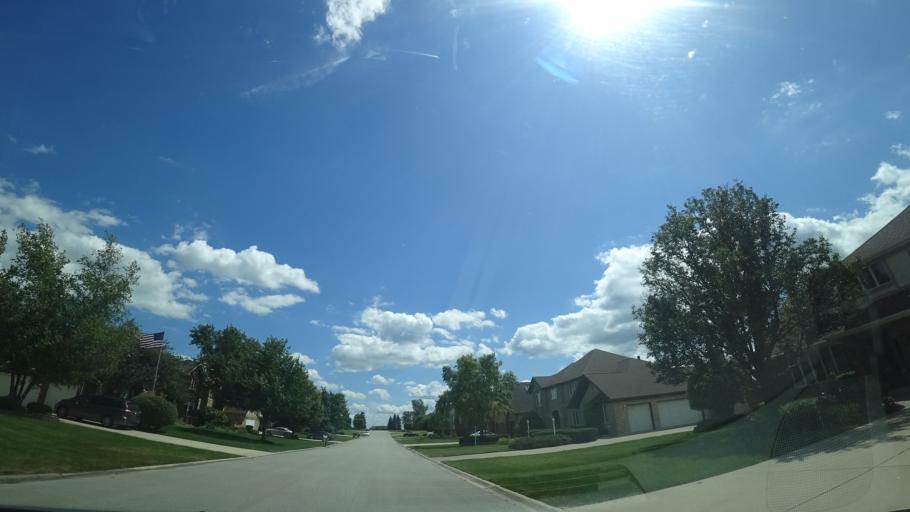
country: US
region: Illinois
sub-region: Will County
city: Homer Glen
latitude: 41.5807
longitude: -87.9110
